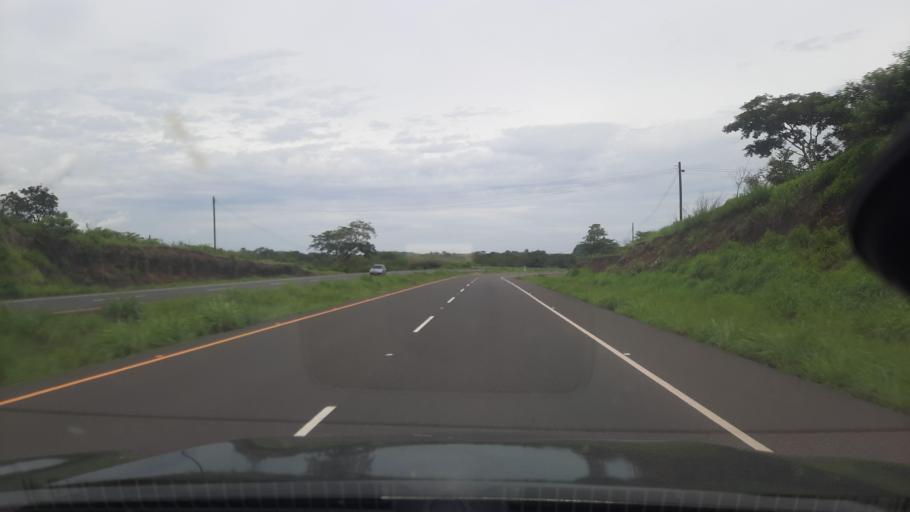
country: HN
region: Valle
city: Aramecina
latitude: 13.7612
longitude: -87.7087
